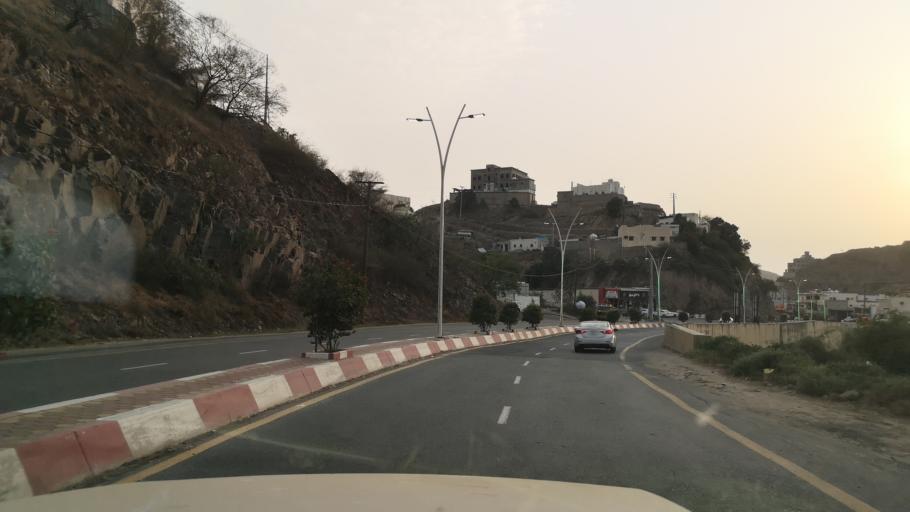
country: YE
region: Sa'dah
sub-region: Monabbih
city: Suq al Khamis
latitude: 17.3402
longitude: 43.1404
